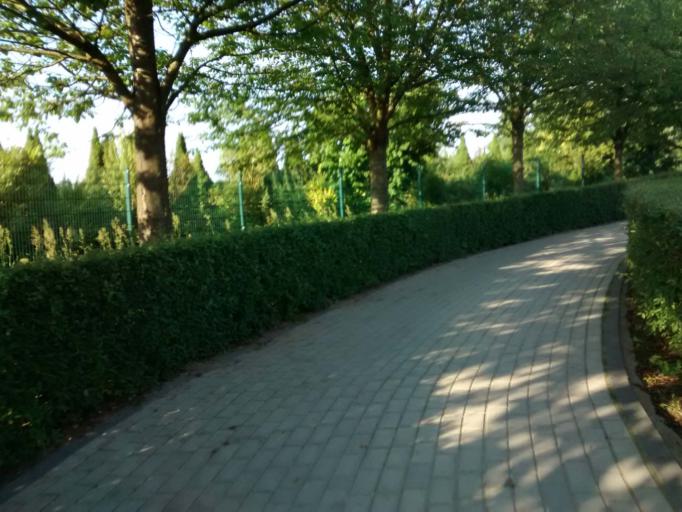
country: DE
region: Brandenburg
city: Hohen Neuendorf
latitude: 52.6525
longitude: 13.2551
